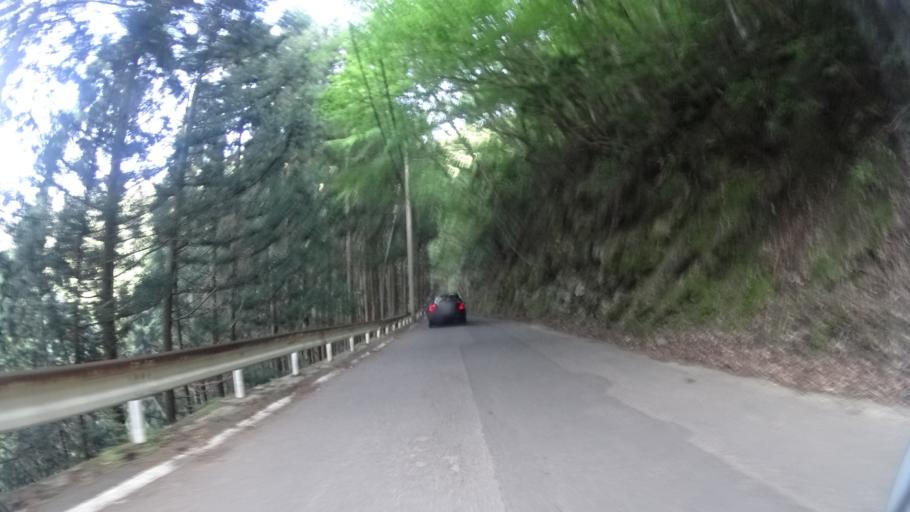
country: JP
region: Tokushima
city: Ikedacho
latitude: 33.9056
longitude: 133.8120
